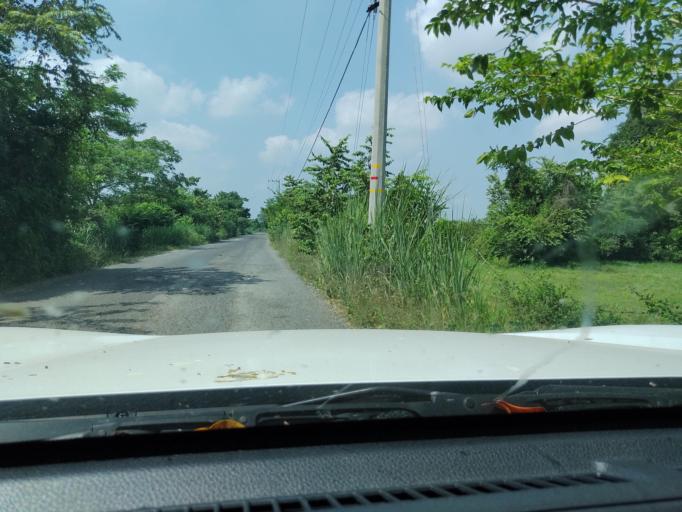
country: MX
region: Veracruz
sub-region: Atzalan
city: Colonias Pedernales
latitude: 20.0640
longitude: -97.0232
